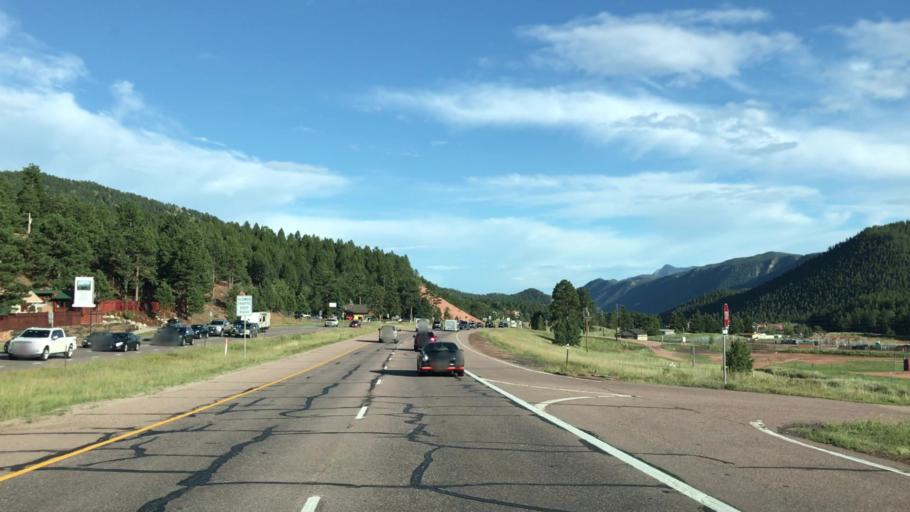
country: US
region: Colorado
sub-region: Teller County
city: Woodland Park
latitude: 38.9805
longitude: -105.0436
